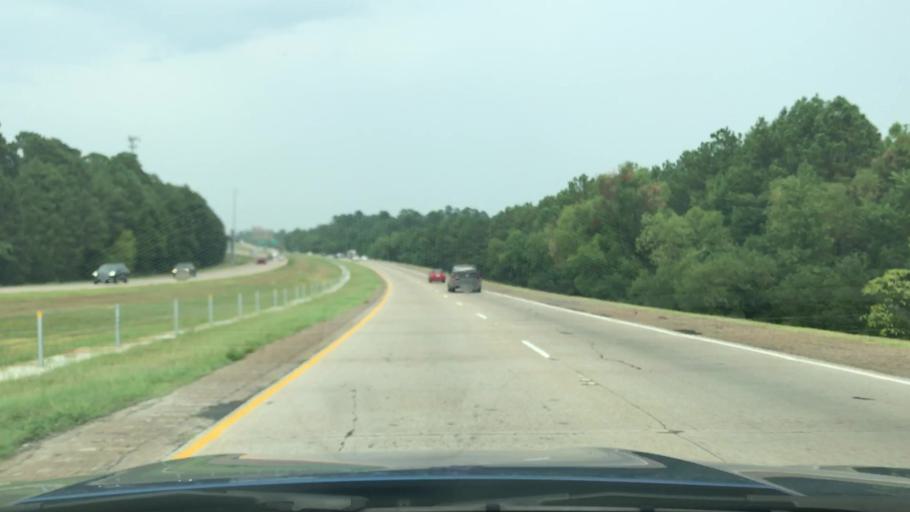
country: US
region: Louisiana
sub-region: Caddo Parish
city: Shreveport
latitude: 32.4178
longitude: -93.8265
